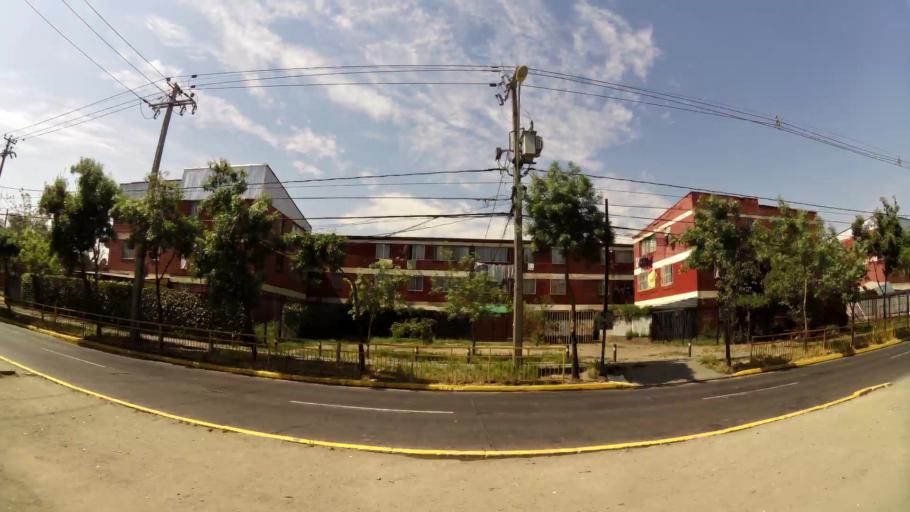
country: CL
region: Santiago Metropolitan
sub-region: Provincia de Santiago
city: La Pintana
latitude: -33.5570
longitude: -70.6696
